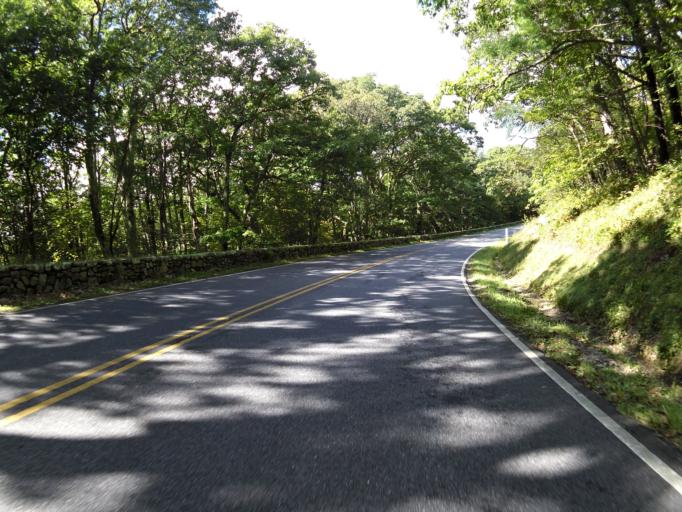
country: US
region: Virginia
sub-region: Page County
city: Luray
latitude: 38.5855
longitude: -78.3684
